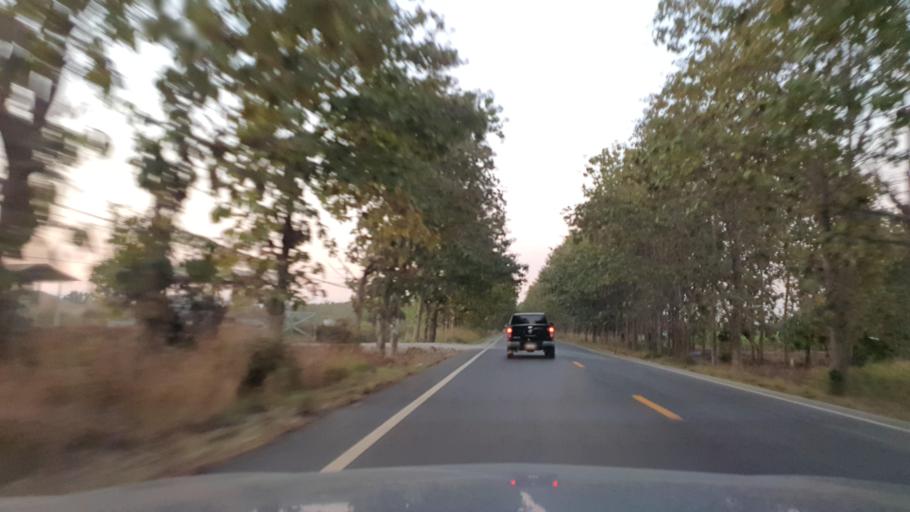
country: TH
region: Phayao
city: Dok Kham Tai
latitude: 19.1088
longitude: 100.0492
